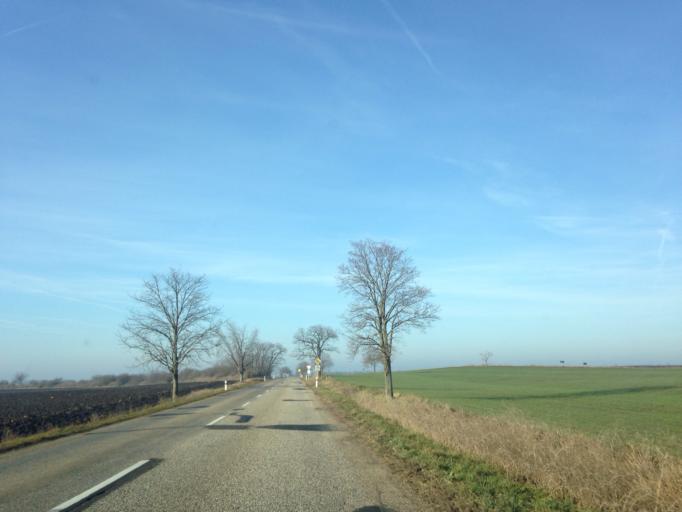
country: SK
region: Nitriansky
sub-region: Okres Nove Zamky
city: Nove Zamky
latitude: 47.9892
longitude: 18.3333
